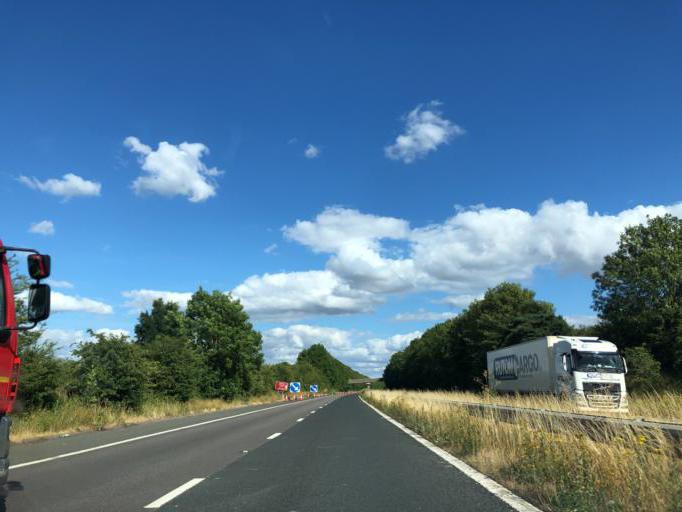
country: GB
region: England
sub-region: Warwickshire
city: Rugby
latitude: 52.3368
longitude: -1.2036
